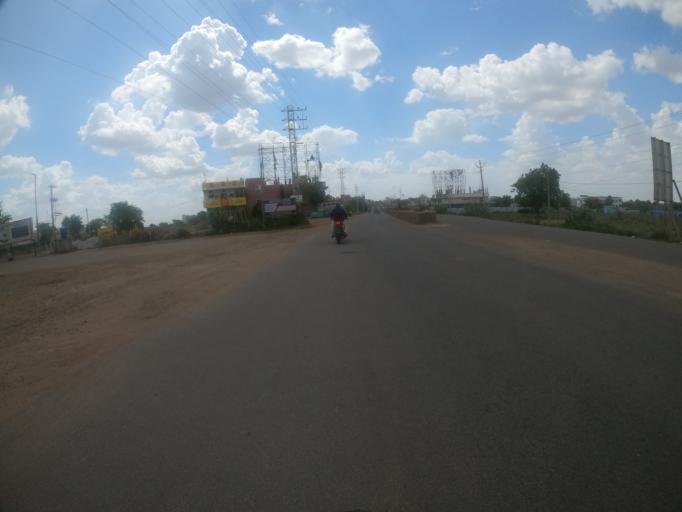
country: IN
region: Telangana
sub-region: Rangareddi
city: Sriramnagar
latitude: 17.3060
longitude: 78.1450
